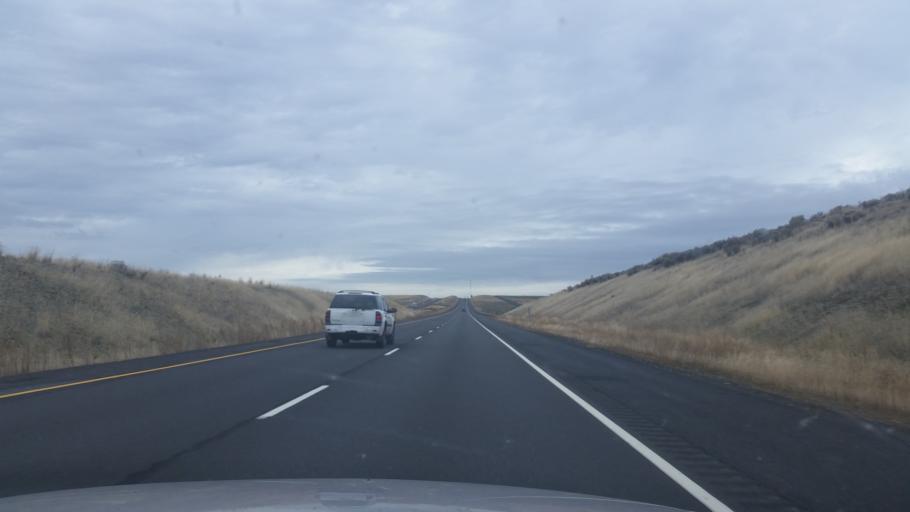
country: US
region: Washington
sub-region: Adams County
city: Ritzville
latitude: 47.0969
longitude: -118.6417
